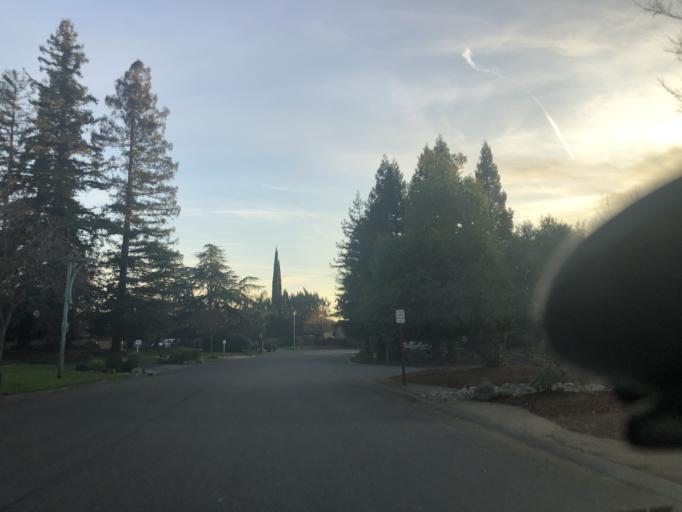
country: US
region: California
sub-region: Sacramento County
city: Gold River
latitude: 38.6381
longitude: -121.2269
